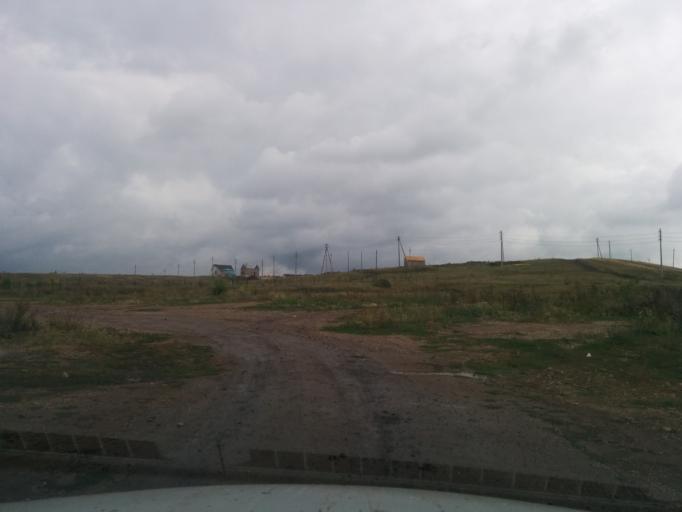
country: RU
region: Bashkortostan
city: Oktyabr'skiy
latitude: 54.4769
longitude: 53.5337
